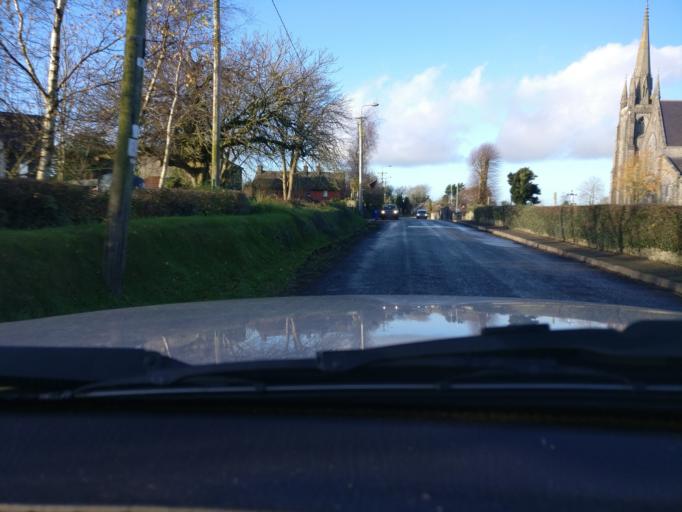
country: IE
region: Leinster
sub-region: An Mhi
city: Athboy
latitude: 53.6914
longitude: -6.9951
